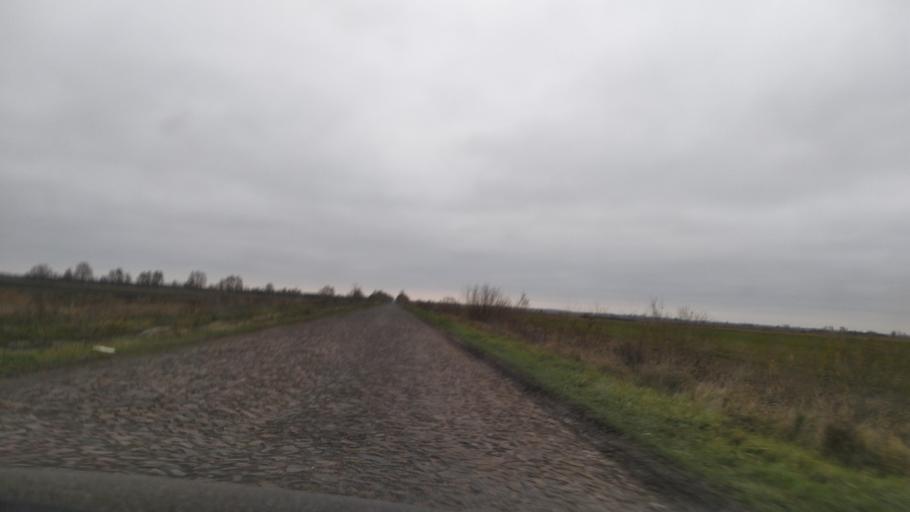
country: BY
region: Brest
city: Davyd-Haradok
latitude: 52.0077
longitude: 27.2055
